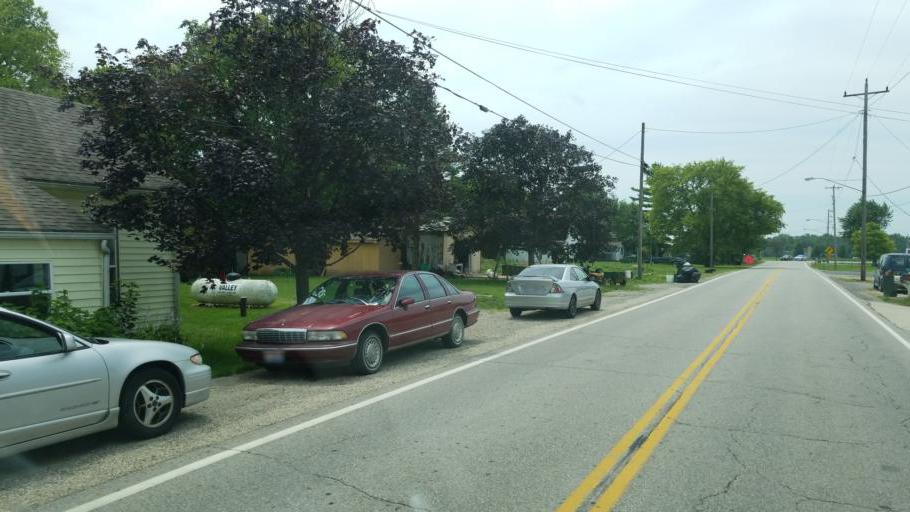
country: US
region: Ohio
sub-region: Madison County
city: Plain City
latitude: 40.0661
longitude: -83.2513
